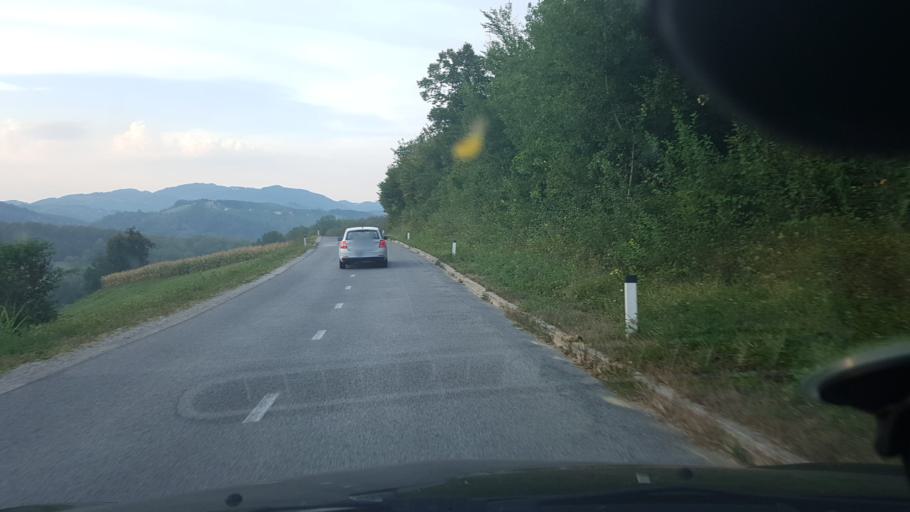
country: SI
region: Kozje
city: Kozje
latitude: 46.0966
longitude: 15.5673
